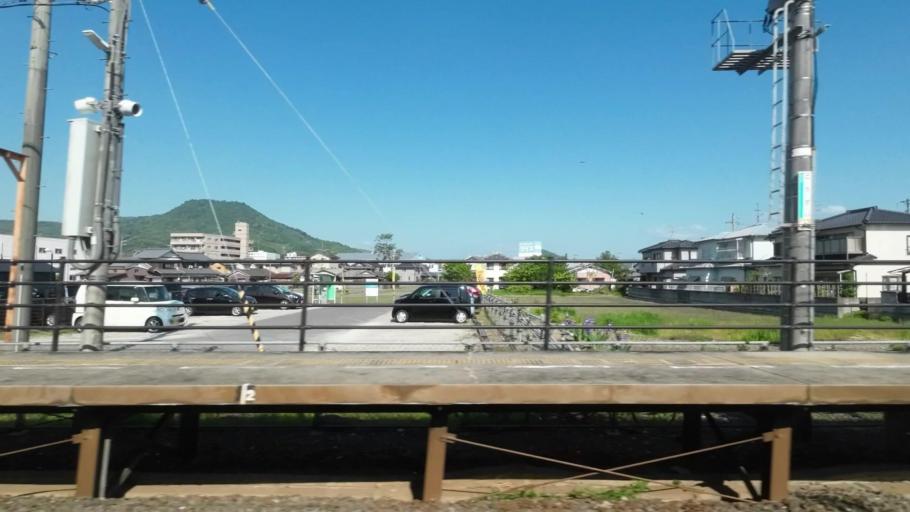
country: JP
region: Kagawa
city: Takamatsu-shi
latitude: 34.3412
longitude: 134.0098
